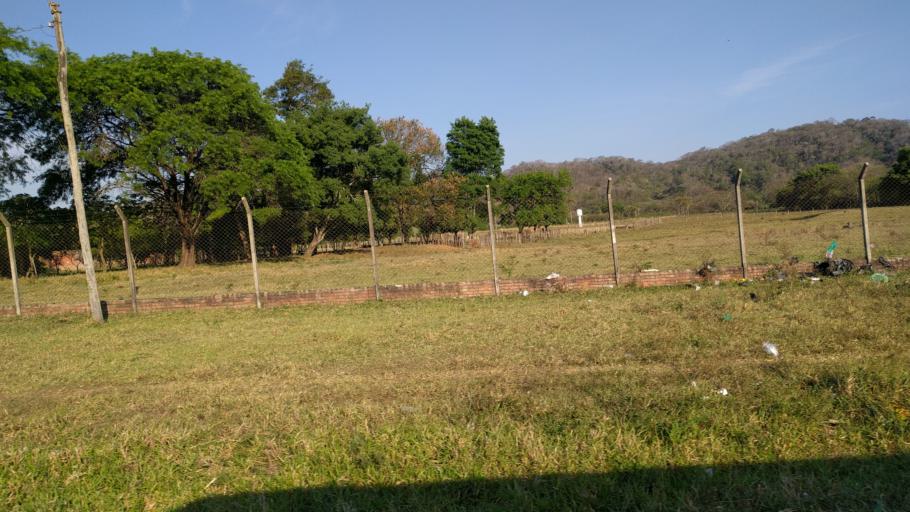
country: BO
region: Santa Cruz
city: Jorochito
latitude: -18.1043
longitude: -63.4557
